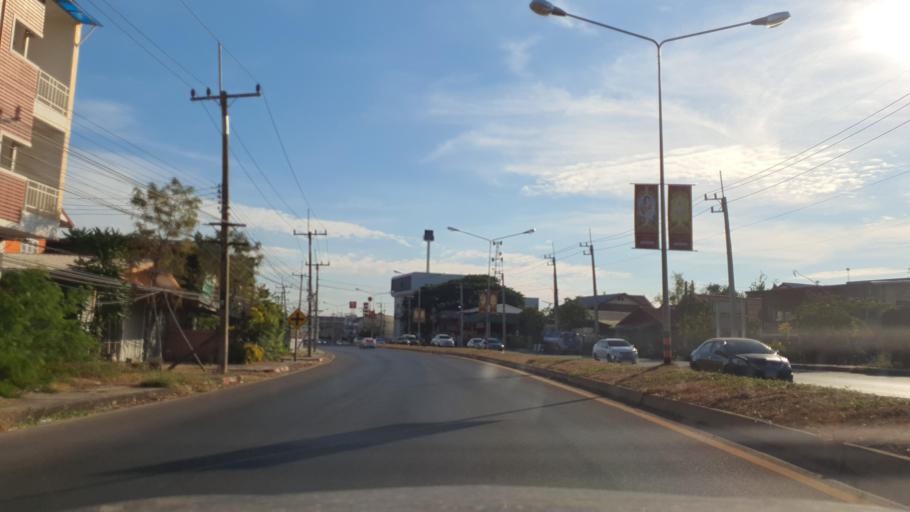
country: TH
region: Maha Sarakham
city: Kantharawichai
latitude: 16.3271
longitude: 103.2994
